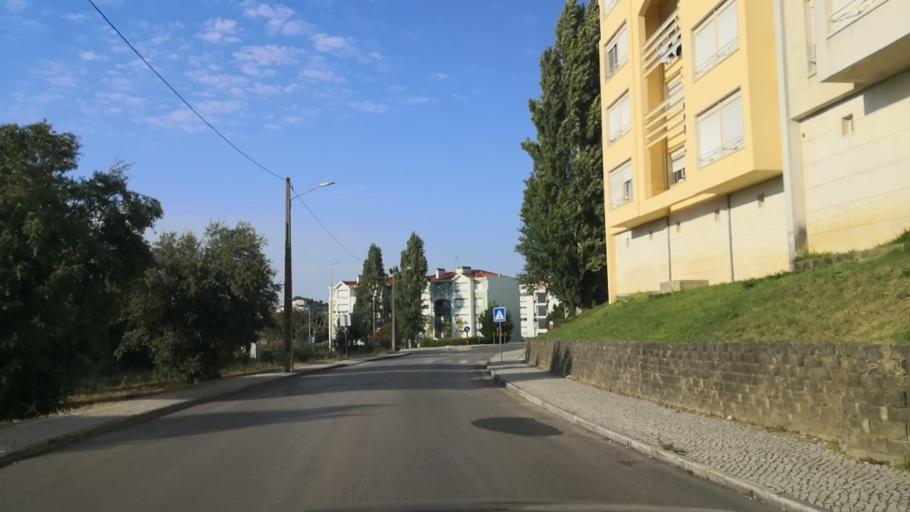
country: PT
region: Santarem
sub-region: Santarem
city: Santarem
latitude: 39.2486
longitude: -8.6879
